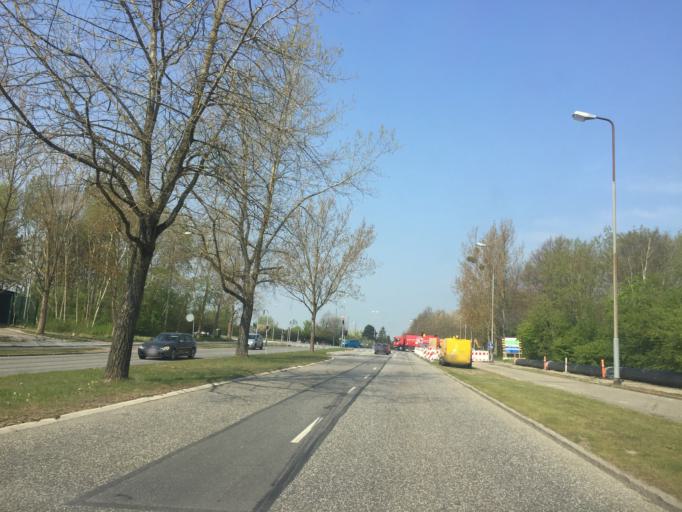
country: DK
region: Capital Region
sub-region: Herlev Kommune
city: Herlev
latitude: 55.6993
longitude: 12.4203
